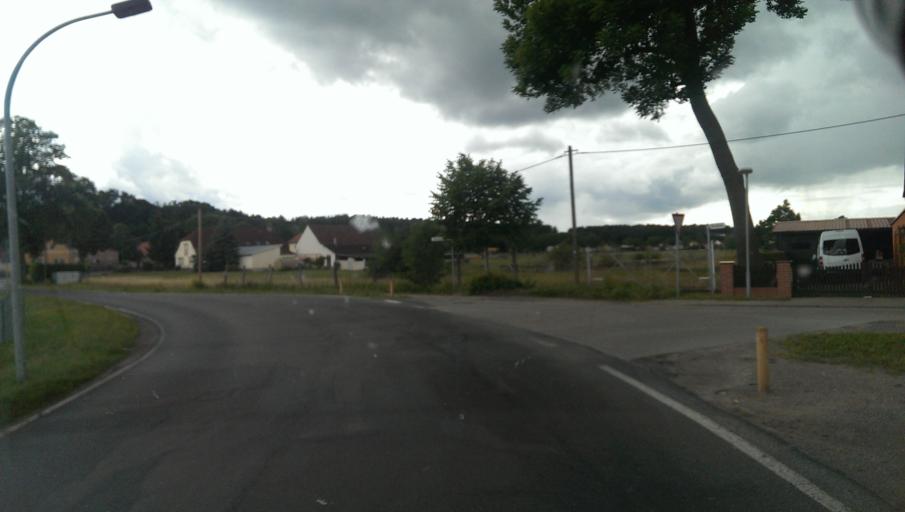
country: DE
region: Brandenburg
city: Borkwalde
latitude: 52.2875
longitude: 12.8386
